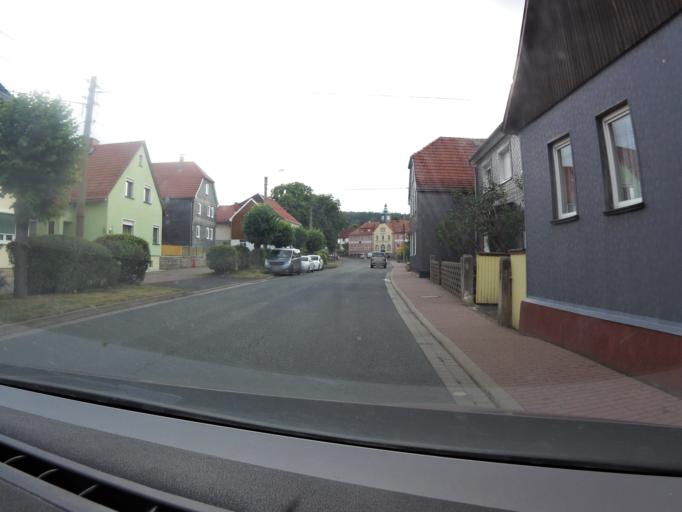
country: DE
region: Thuringia
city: Martinroda
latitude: 50.7263
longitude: 10.8879
